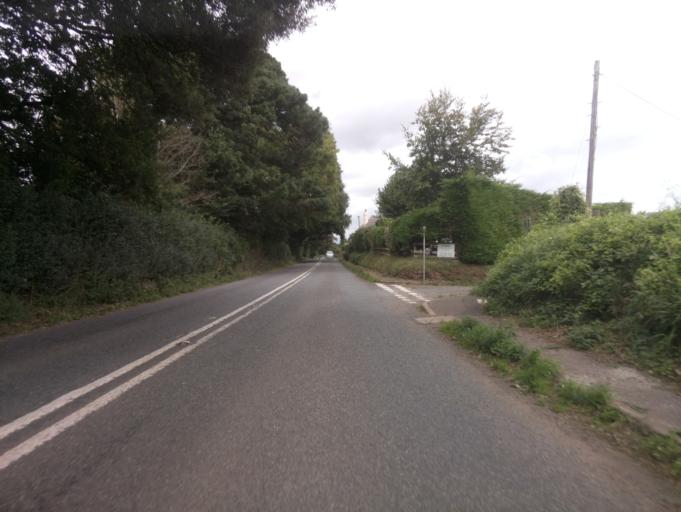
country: GB
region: England
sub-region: Devon
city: Bradninch
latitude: 50.7740
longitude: -3.4411
